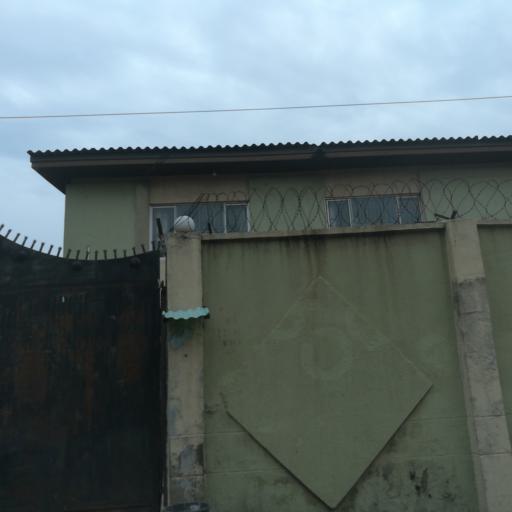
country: NG
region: Lagos
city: Ikeja
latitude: 6.5993
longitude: 3.3471
